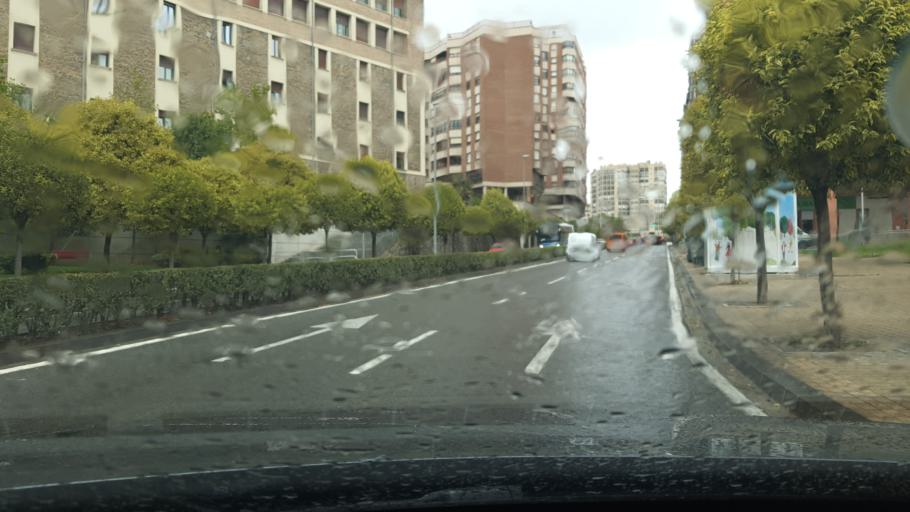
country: ES
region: Navarre
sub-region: Provincia de Navarra
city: Segundo Ensanche
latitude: 42.8066
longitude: -1.6441
